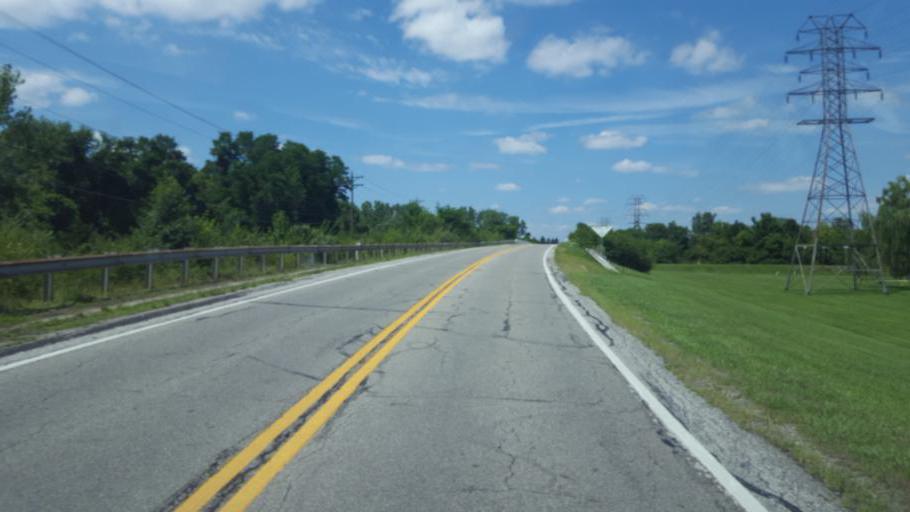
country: US
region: Ohio
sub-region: Franklin County
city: Obetz
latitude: 39.8719
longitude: -82.9887
